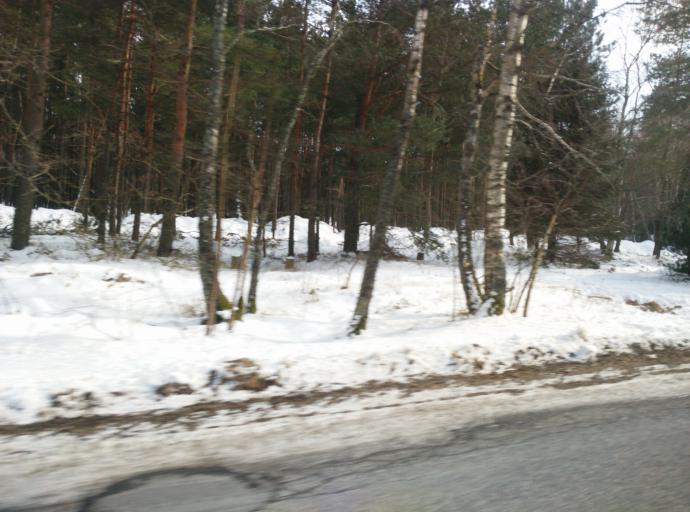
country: LT
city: Nida
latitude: 55.1223
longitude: 20.7708
